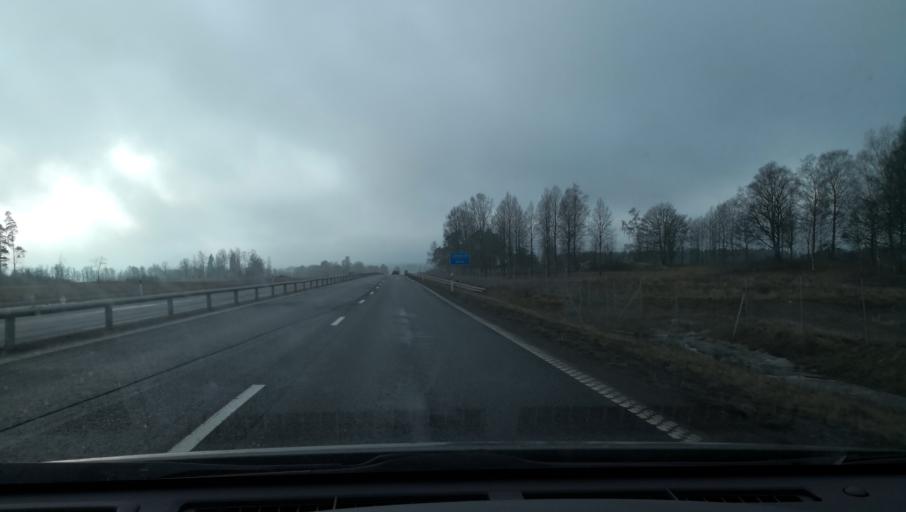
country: SE
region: Vaestra Goetaland
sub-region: Gullspangs Kommun
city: Anderstorp
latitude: 58.8717
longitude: 14.2471
